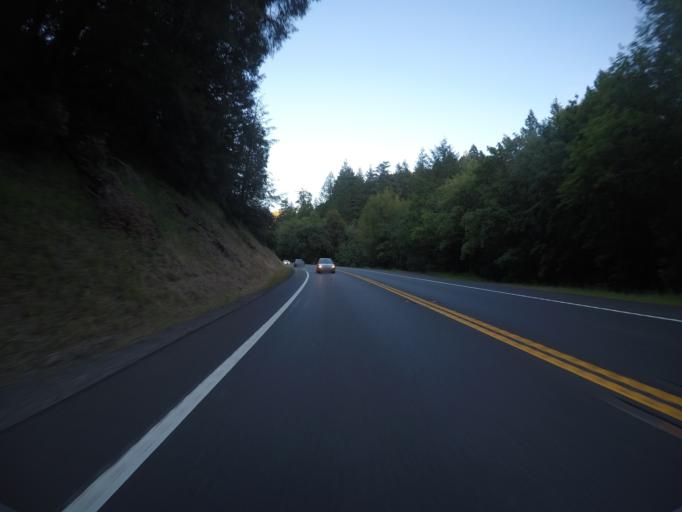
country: US
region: California
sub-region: Mendocino County
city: Laytonville
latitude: 39.8098
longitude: -123.5541
